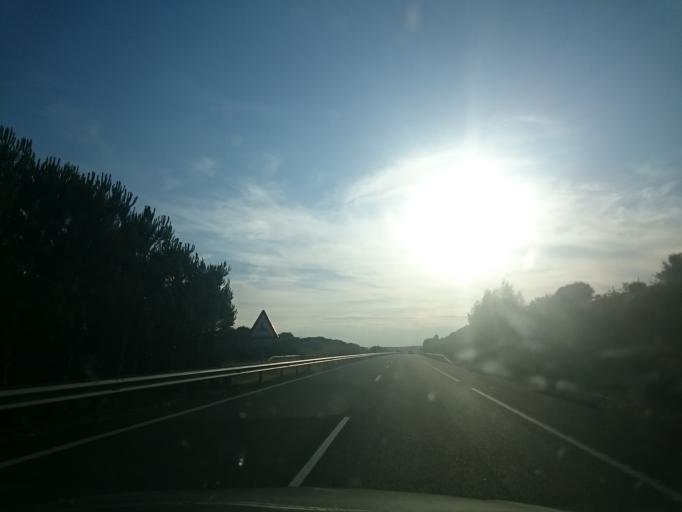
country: ES
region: Castille and Leon
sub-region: Provincia de Palencia
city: Moratinos
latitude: 42.3639
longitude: -4.9342
